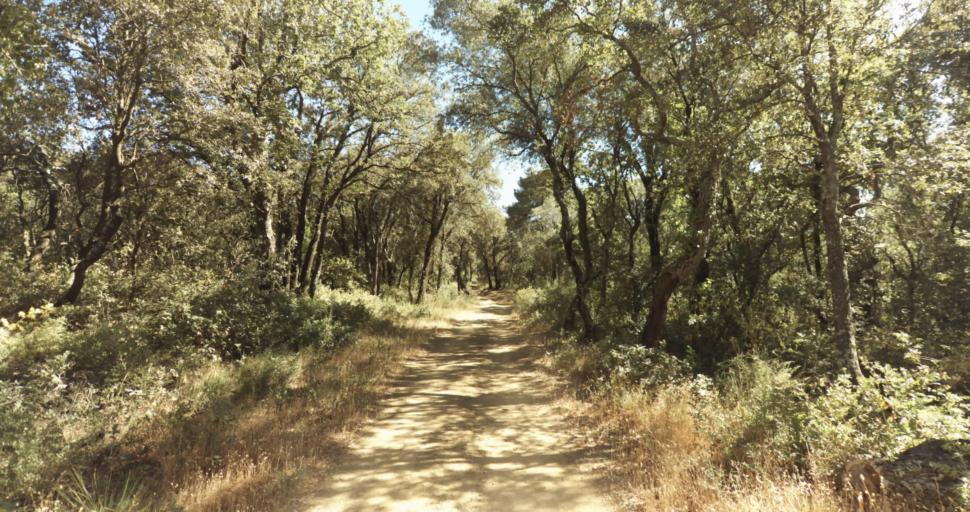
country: FR
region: Provence-Alpes-Cote d'Azur
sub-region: Departement du Var
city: Gassin
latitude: 43.2449
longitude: 6.5845
